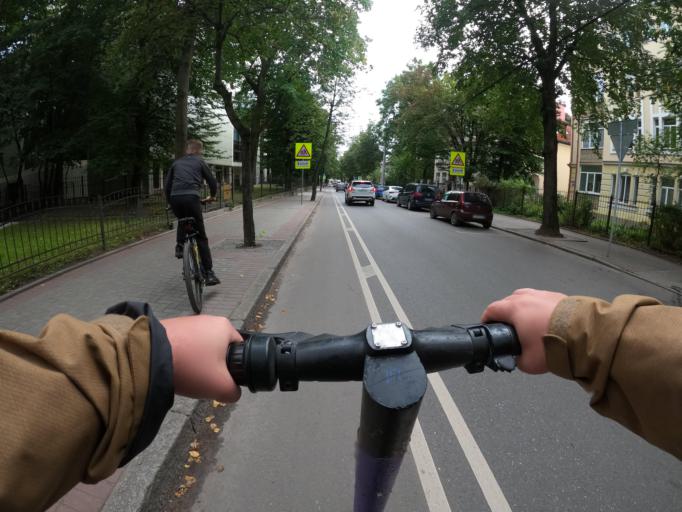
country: RU
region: Kaliningrad
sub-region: Gorod Kaliningrad
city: Kaliningrad
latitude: 54.7261
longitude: 20.4789
